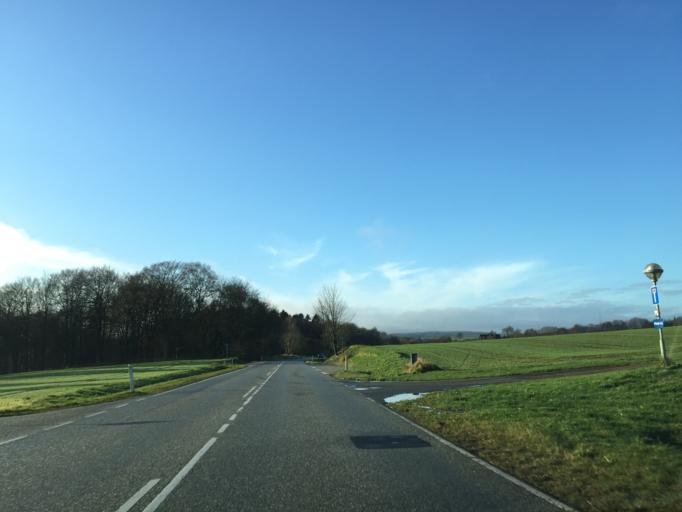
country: DK
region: Central Jutland
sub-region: Skanderborg Kommune
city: Galten
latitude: 56.1743
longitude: 9.8536
